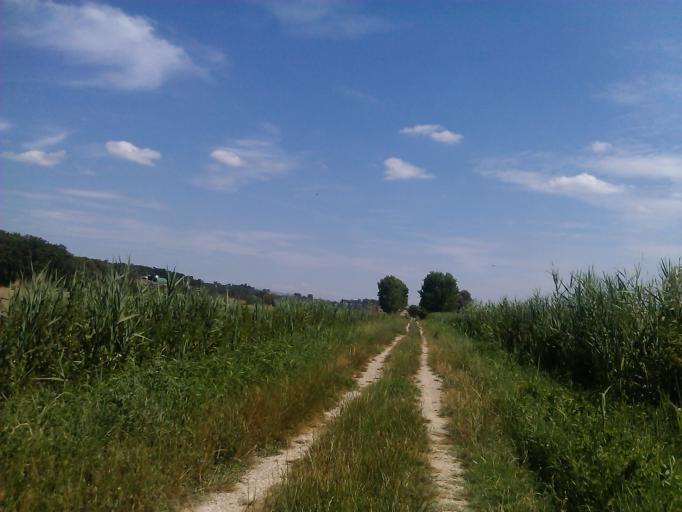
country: IT
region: Umbria
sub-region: Provincia di Perugia
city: Pozzuolo
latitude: 43.0730
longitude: 11.9248
